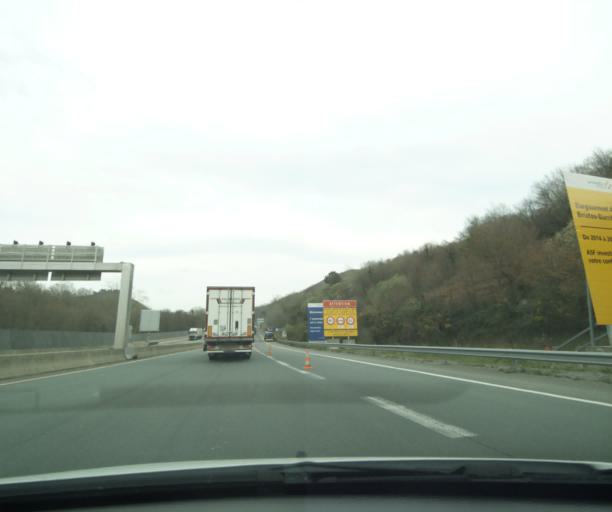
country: FR
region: Aquitaine
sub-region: Departement des Pyrenees-Atlantiques
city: Hendaye
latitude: 43.3414
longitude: -1.7465
